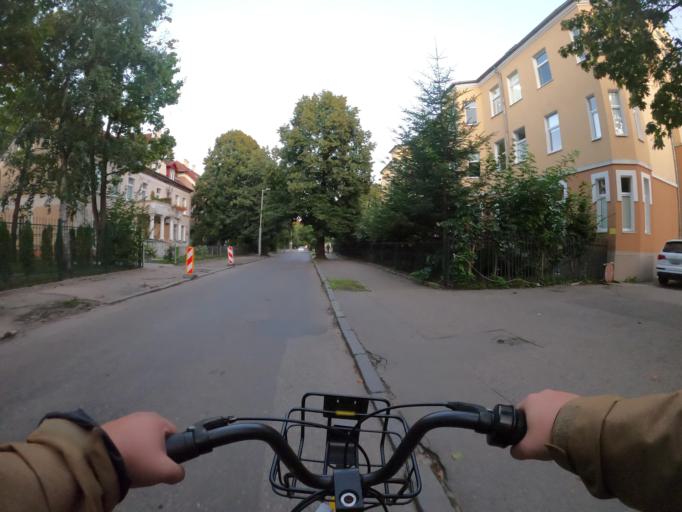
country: RU
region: Kaliningrad
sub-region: Gorod Kaliningrad
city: Kaliningrad
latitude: 54.7268
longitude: 20.4797
